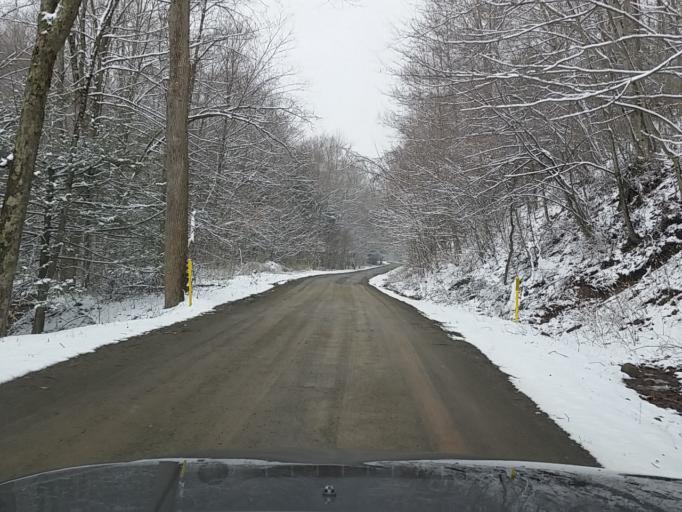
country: US
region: Pennsylvania
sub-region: Sullivan County
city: Laporte
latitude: 41.3213
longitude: -76.4504
